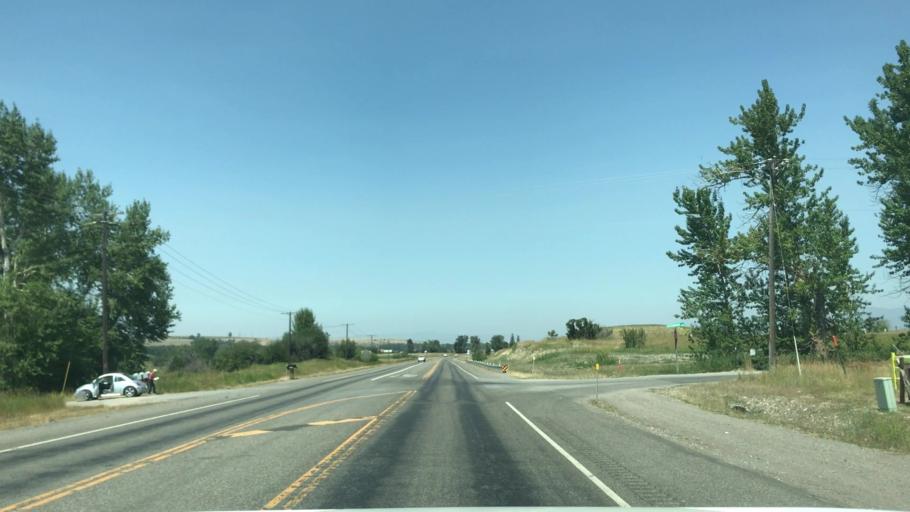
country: US
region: Montana
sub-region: Gallatin County
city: Four Corners
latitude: 45.6124
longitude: -111.1962
